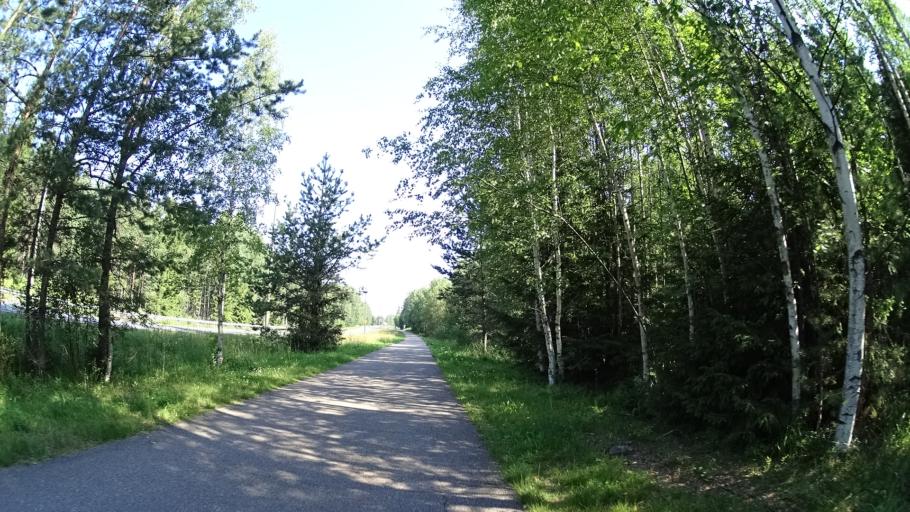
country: FI
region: Uusimaa
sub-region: Helsinki
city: Kerava
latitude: 60.3333
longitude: 25.1249
